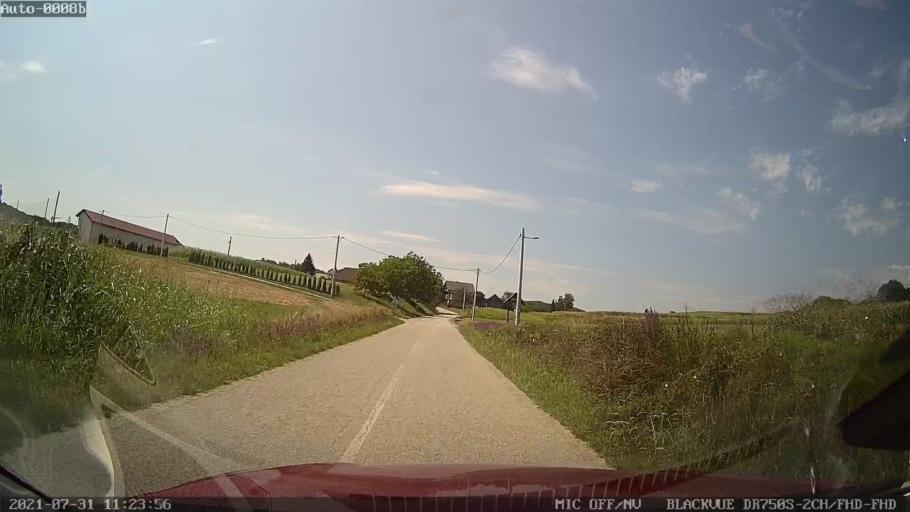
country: HR
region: Varazdinska
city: Jalzabet
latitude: 46.2132
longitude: 16.4594
